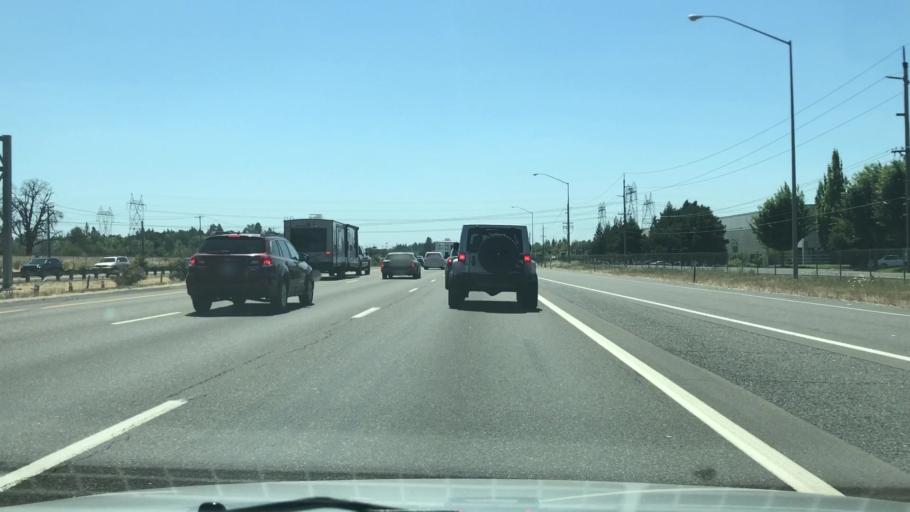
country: US
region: Oregon
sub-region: Clackamas County
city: Wilsonville
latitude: 45.3321
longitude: -122.7698
